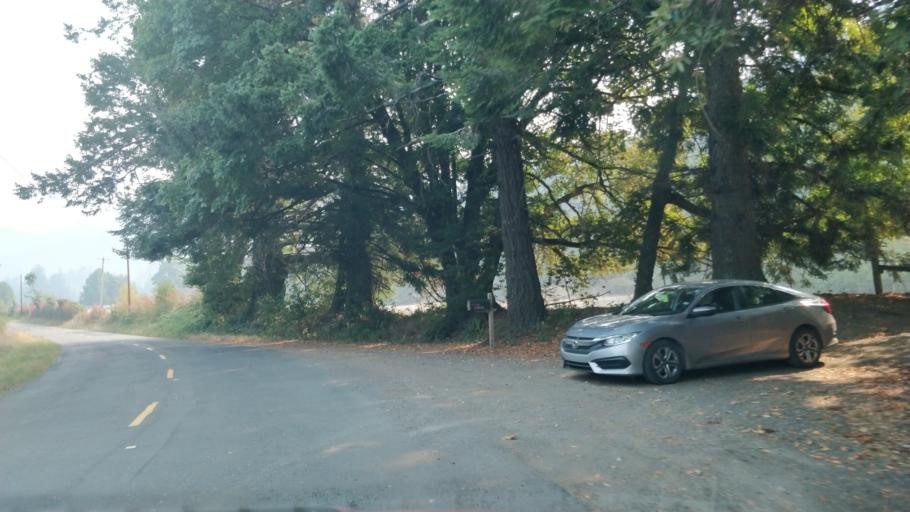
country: US
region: California
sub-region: Humboldt County
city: Rio Dell
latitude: 40.2813
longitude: -124.2492
